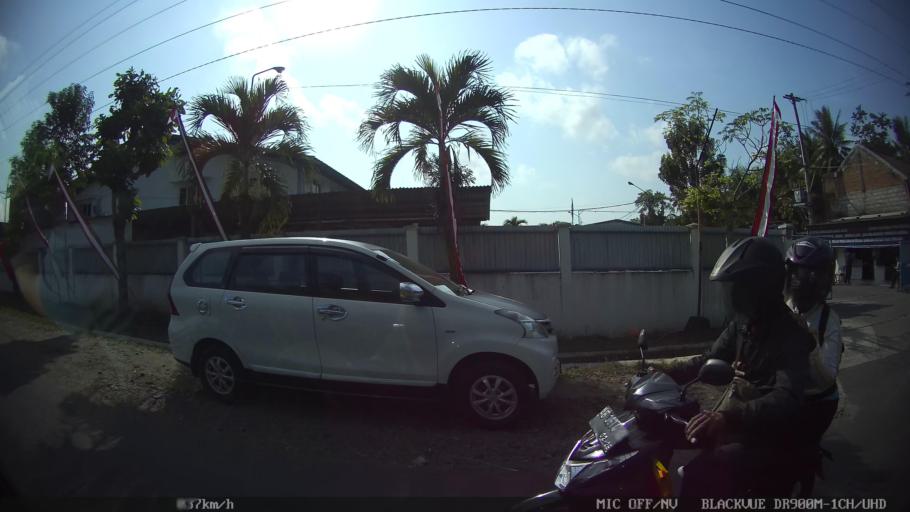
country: ID
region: Daerah Istimewa Yogyakarta
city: Gamping Lor
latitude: -7.8115
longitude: 110.2994
